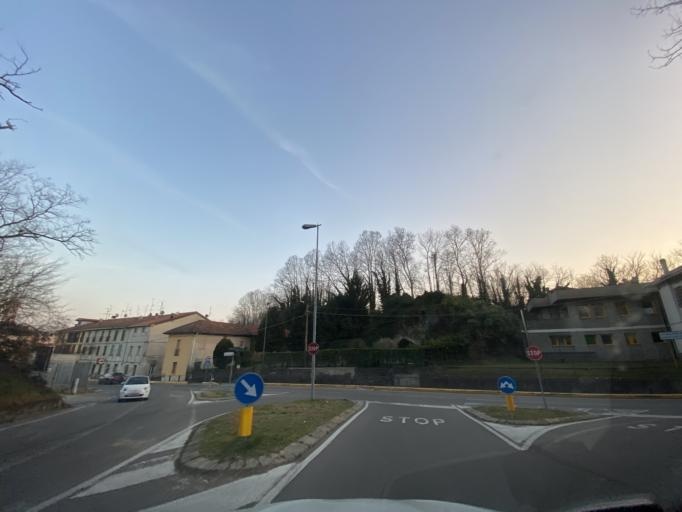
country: IT
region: Lombardy
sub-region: Provincia di Monza e Brianza
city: Limbiate
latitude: 45.6046
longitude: 9.1181
